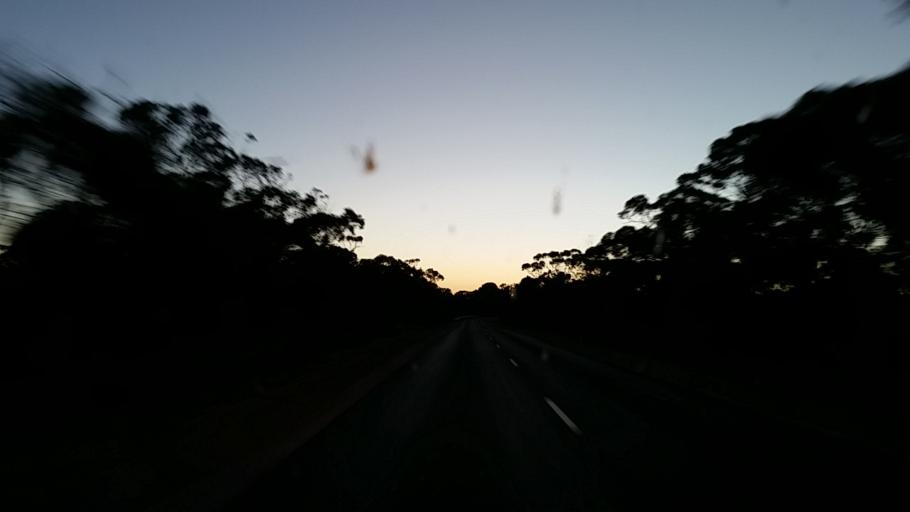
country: AU
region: South Australia
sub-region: Wakefield
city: Balaklava
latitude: -34.1161
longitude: 138.4782
